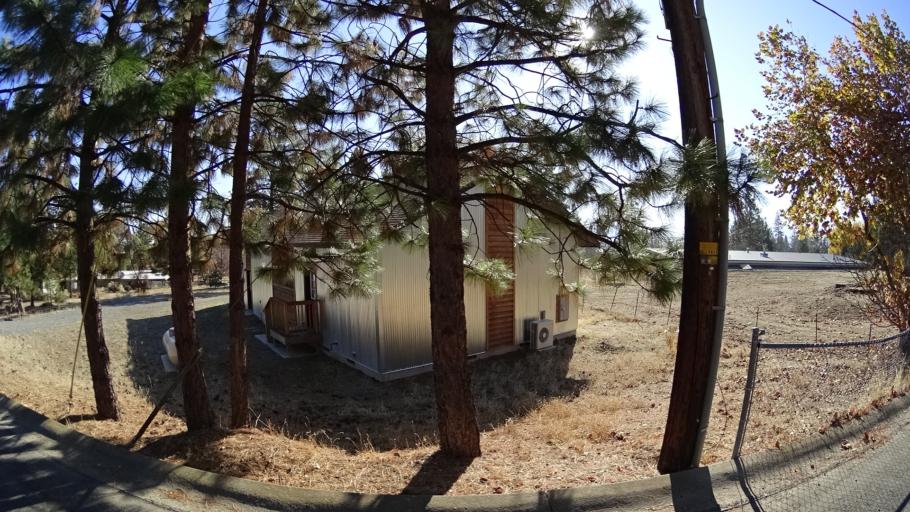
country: US
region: California
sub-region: Siskiyou County
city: Yreka
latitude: 41.7404
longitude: -122.6519
